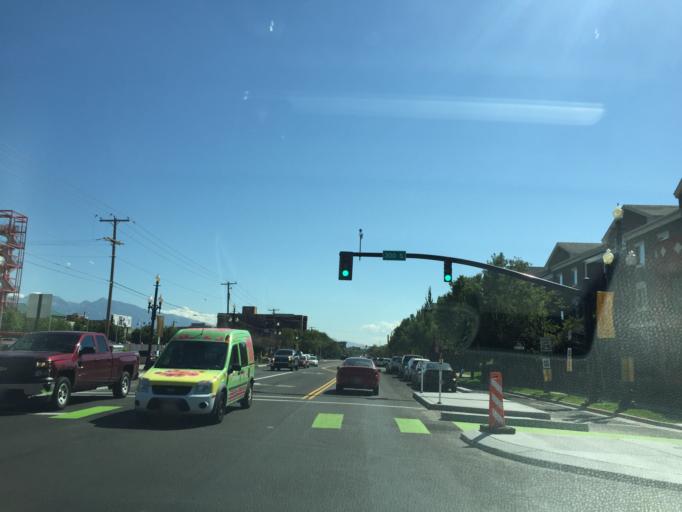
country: US
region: Utah
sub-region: Salt Lake County
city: Salt Lake City
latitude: 40.7628
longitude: -111.8968
